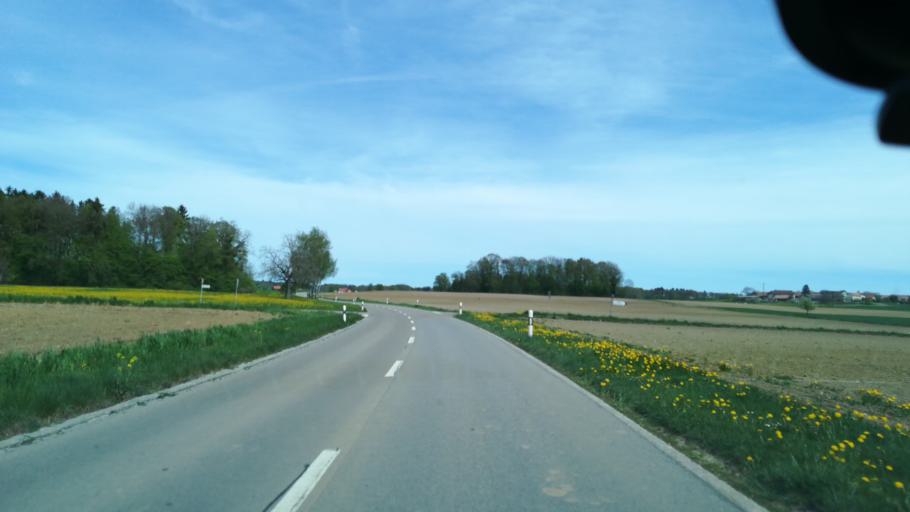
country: CH
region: Thurgau
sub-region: Weinfelden District
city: Maerstetten-Dorf
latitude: 47.6276
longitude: 9.0689
